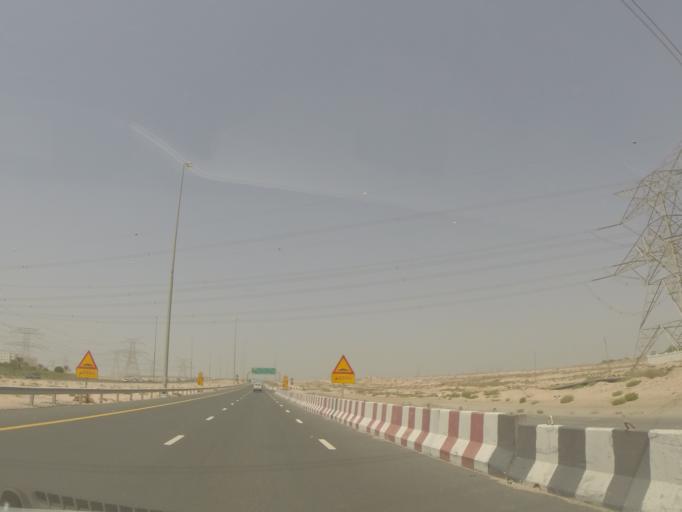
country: AE
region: Dubai
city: Dubai
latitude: 25.0094
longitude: 55.1685
